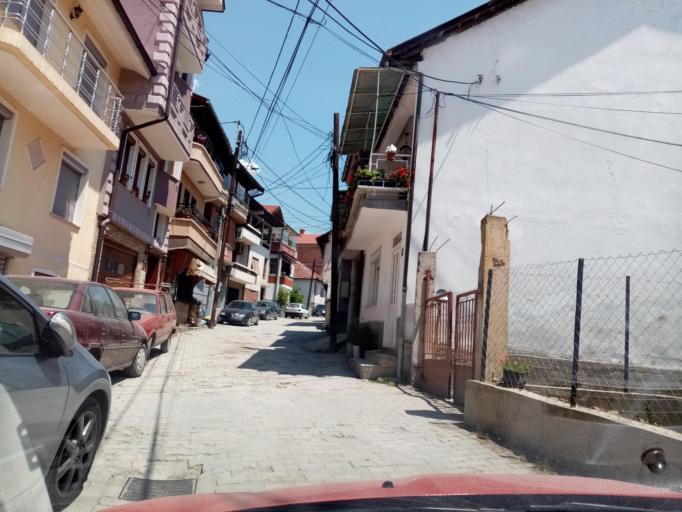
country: MK
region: Tetovo
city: Tetovo
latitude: 42.0155
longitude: 20.9702
